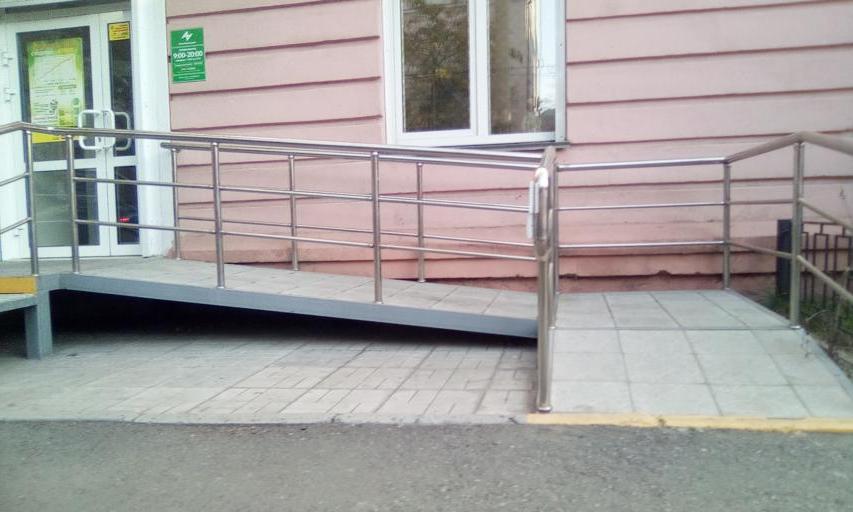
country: RU
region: Chelyabinsk
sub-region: Gorod Chelyabinsk
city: Chelyabinsk
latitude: 55.1580
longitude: 61.3902
